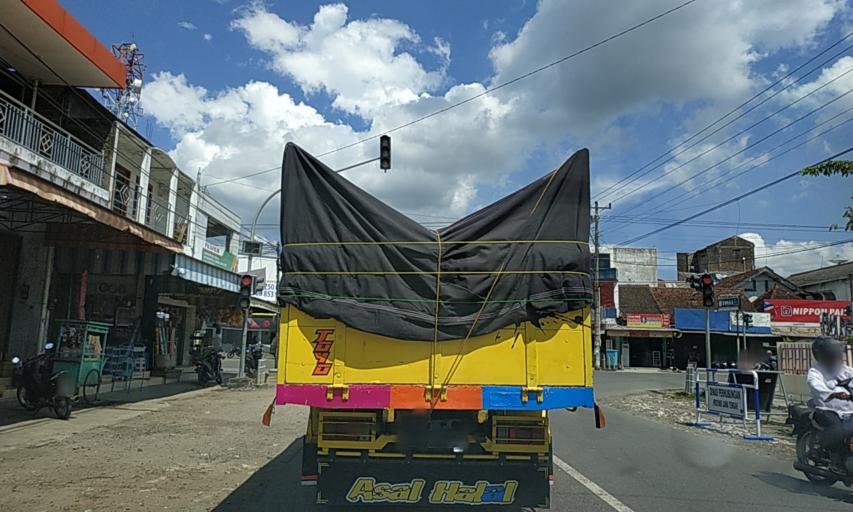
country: ID
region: East Java
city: Ploso
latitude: -7.9794
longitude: 110.9338
